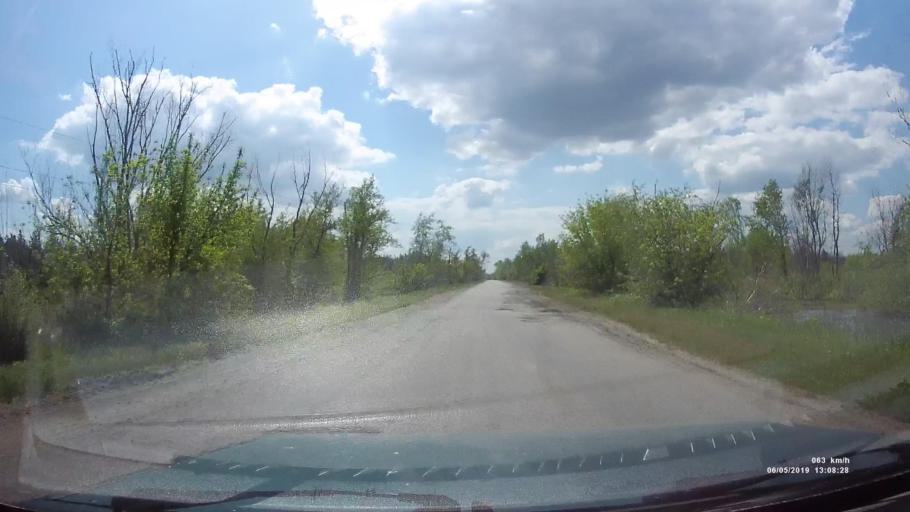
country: RU
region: Rostov
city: Ust'-Donetskiy
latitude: 47.7754
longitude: 40.9950
